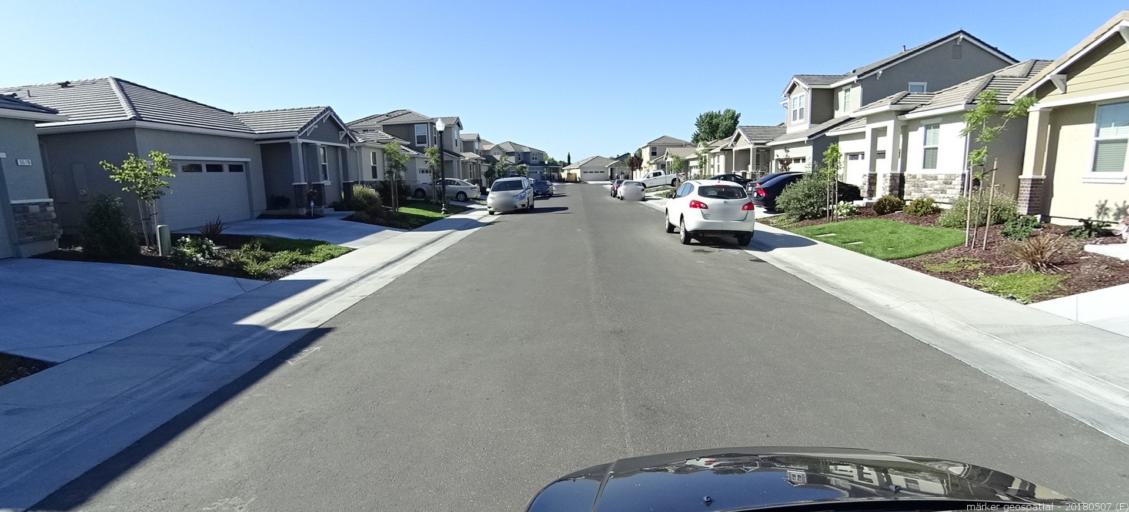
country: US
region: California
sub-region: Sacramento County
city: Rio Linda
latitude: 38.6763
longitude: -121.4939
